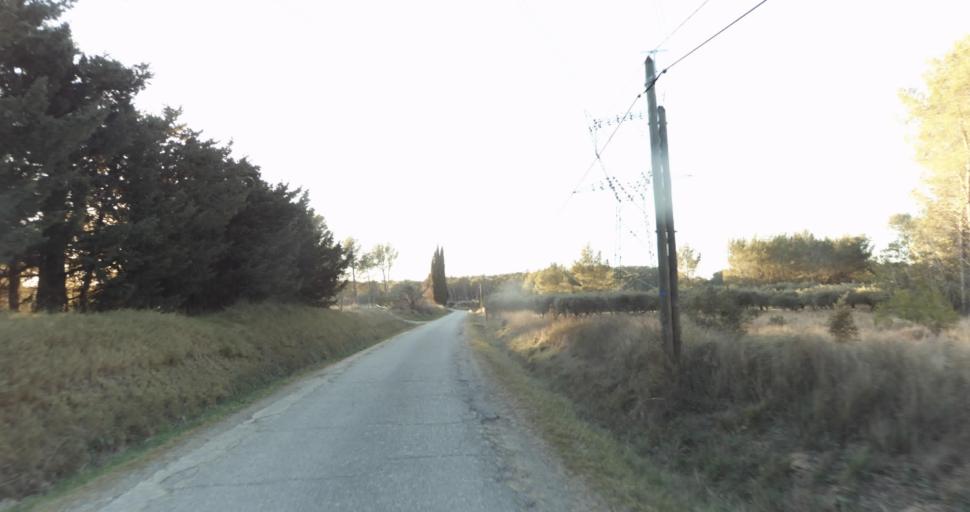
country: FR
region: Provence-Alpes-Cote d'Azur
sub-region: Departement des Bouches-du-Rhone
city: Barbentane
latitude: 43.8844
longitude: 4.7412
